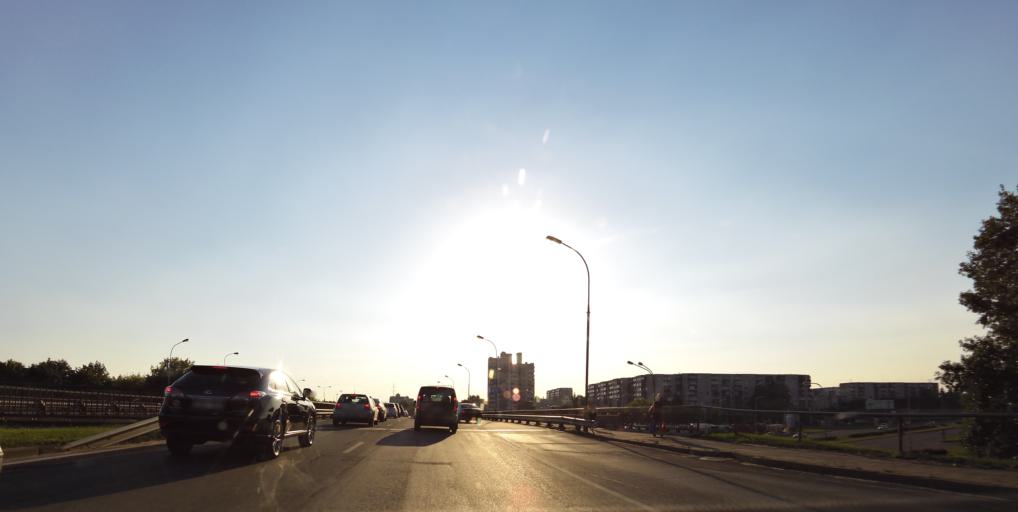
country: LT
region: Vilnius County
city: Seskine
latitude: 54.7103
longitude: 25.2521
